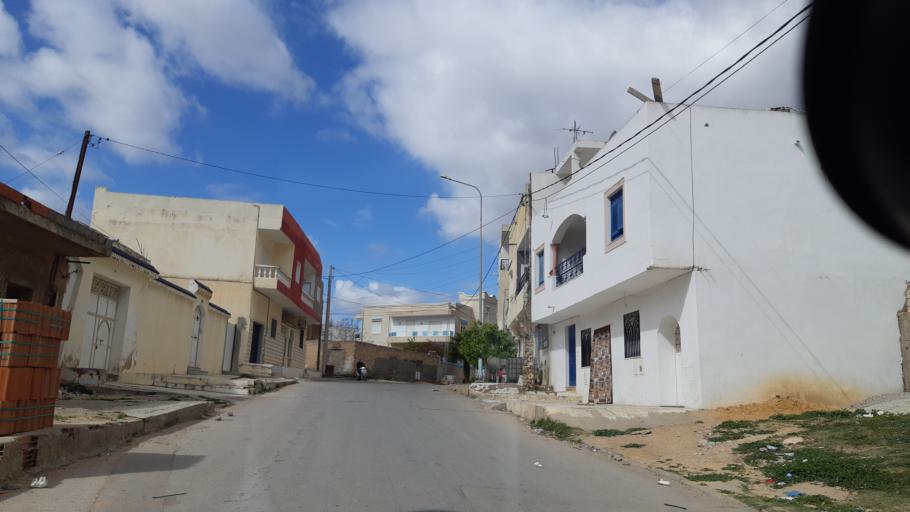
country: TN
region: Susah
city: Akouda
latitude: 35.8725
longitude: 10.5219
